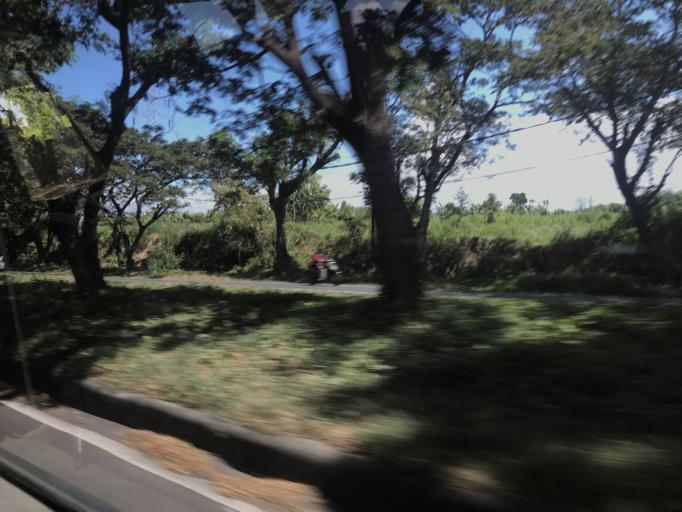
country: ID
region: Bali
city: Dawan
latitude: -8.5569
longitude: 115.4308
